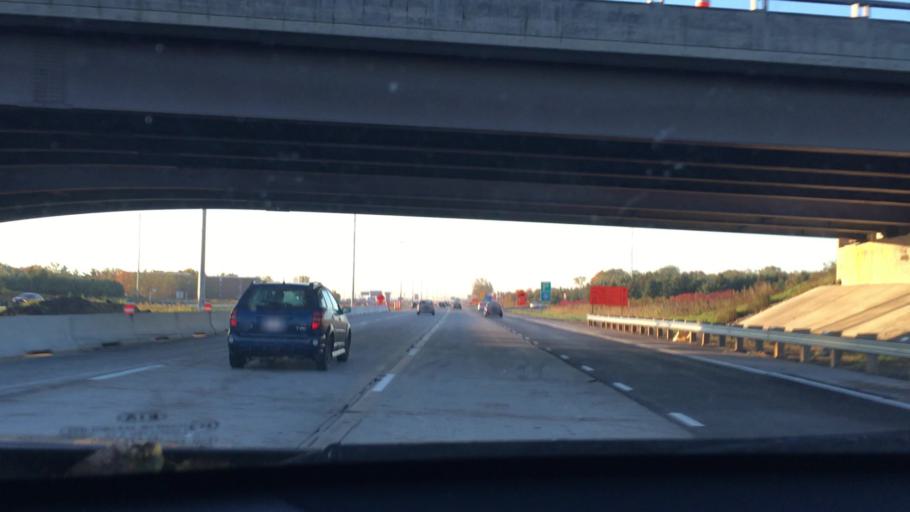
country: CA
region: Quebec
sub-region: Laurentides
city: Saint-Jerome
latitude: 45.7793
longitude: -74.0209
